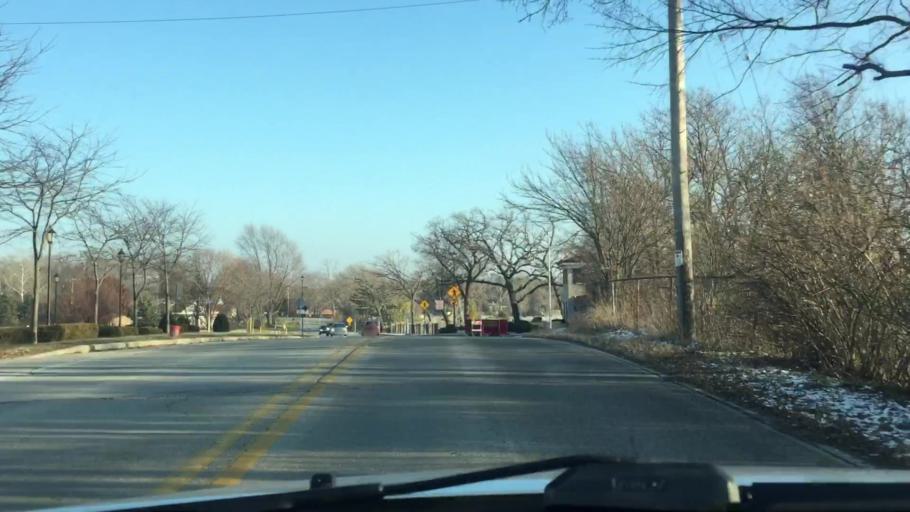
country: US
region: Wisconsin
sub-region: Waukesha County
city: Oconomowoc
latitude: 43.0799
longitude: -88.4905
